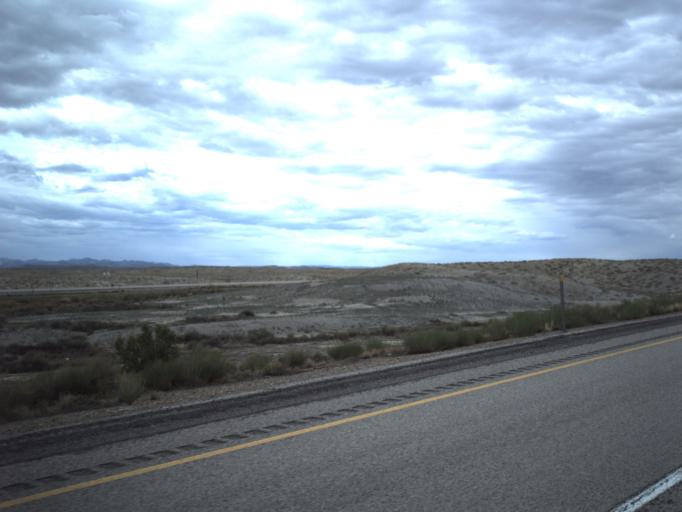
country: US
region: Utah
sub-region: Grand County
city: Moab
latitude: 38.9881
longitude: -109.3361
